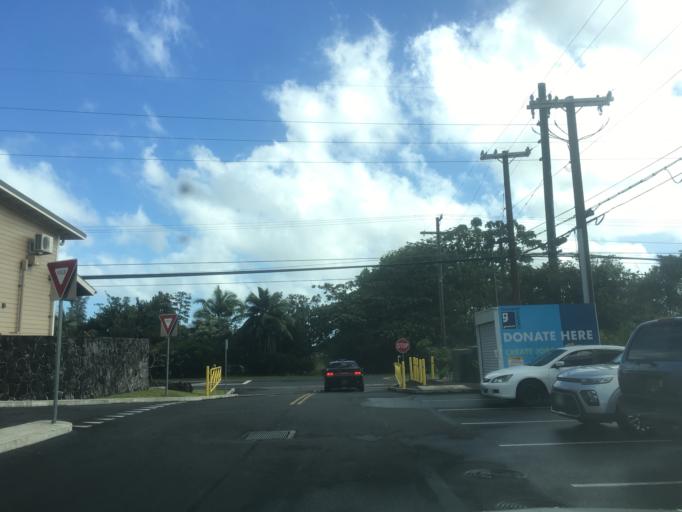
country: US
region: Hawaii
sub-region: Hawaii County
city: Hawaiian Paradise Park
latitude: 19.5021
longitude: -154.9553
